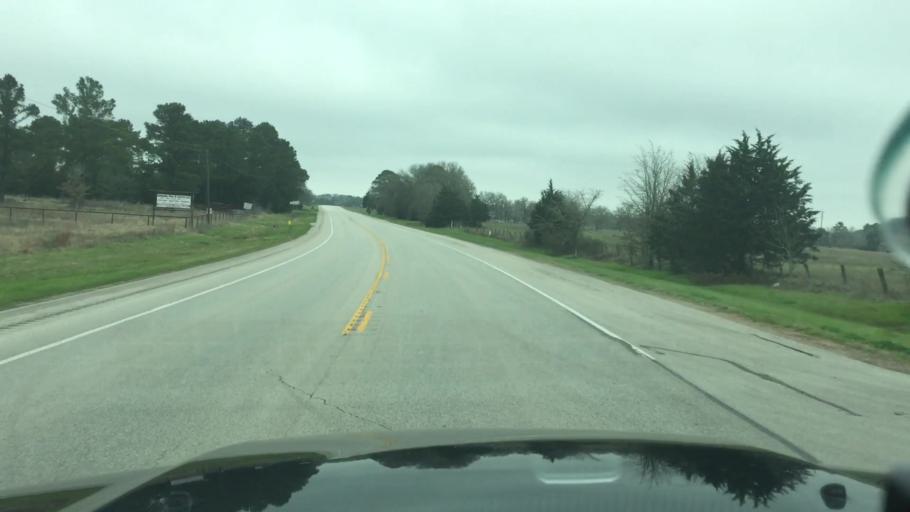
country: US
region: Texas
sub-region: Lee County
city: Giddings
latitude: 30.0565
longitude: -96.9143
